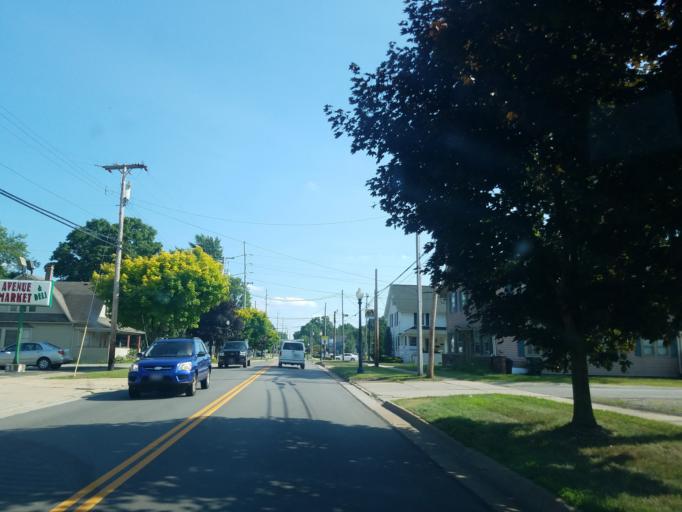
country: US
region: Ohio
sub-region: Summit County
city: Mogadore
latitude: 41.0490
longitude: -81.3932
